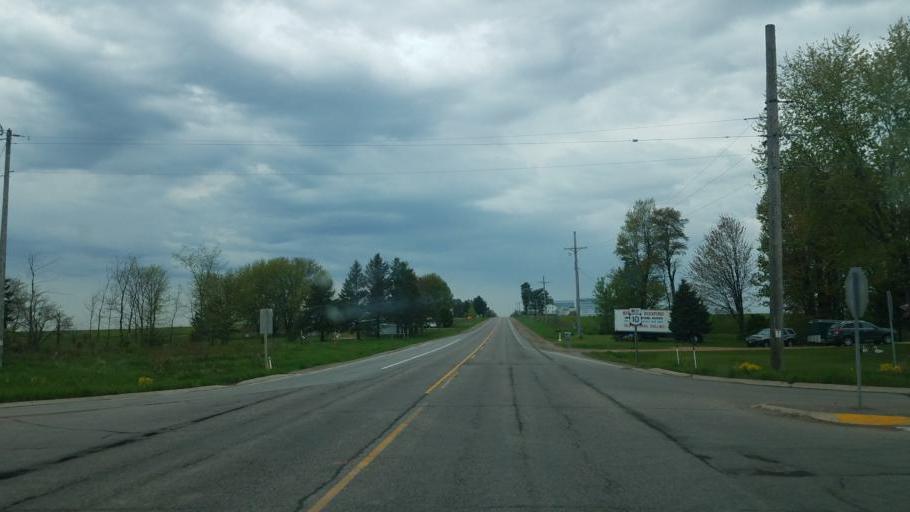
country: US
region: Wisconsin
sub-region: Marathon County
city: Spencer
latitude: 44.5981
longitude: -90.3561
